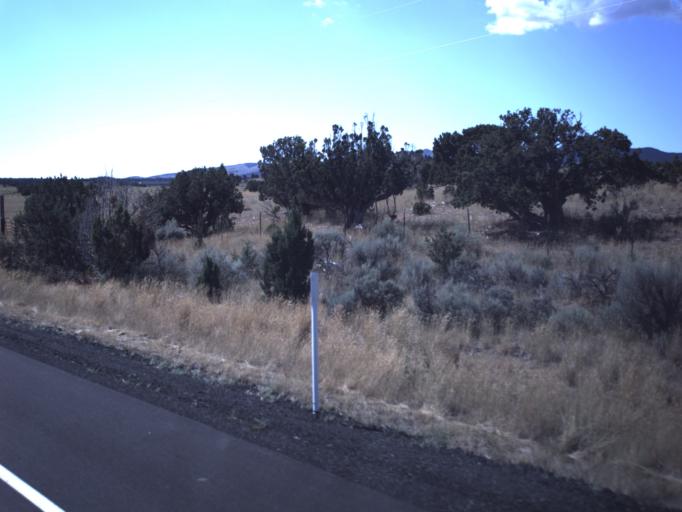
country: US
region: Utah
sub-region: Utah County
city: Eagle Mountain
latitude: 40.0419
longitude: -112.2908
